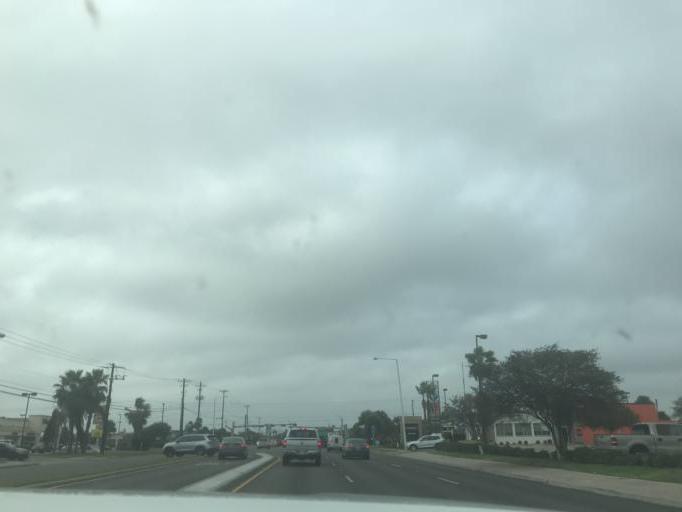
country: US
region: Texas
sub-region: Nueces County
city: Corpus Christi
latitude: 27.6847
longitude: -97.3820
